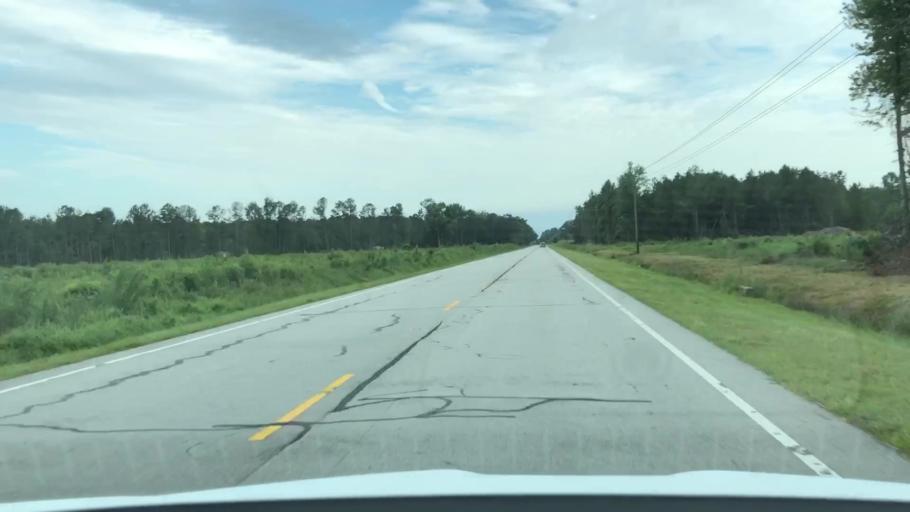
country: US
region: North Carolina
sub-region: Lenoir County
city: Kinston
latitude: 35.1285
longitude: -77.5225
